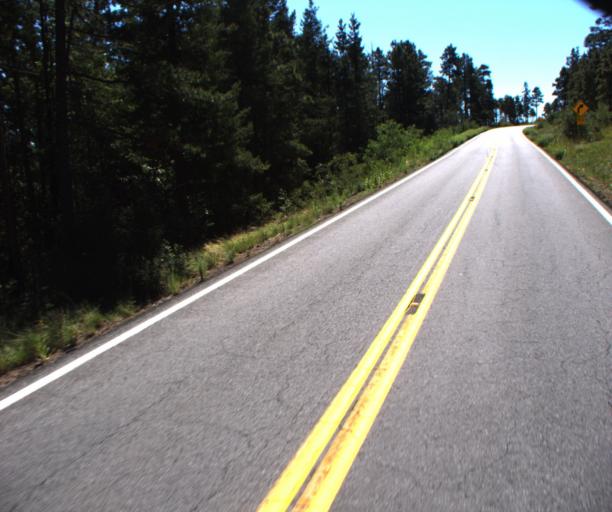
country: US
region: Arizona
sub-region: Apache County
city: Eagar
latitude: 33.7258
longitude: -109.2001
